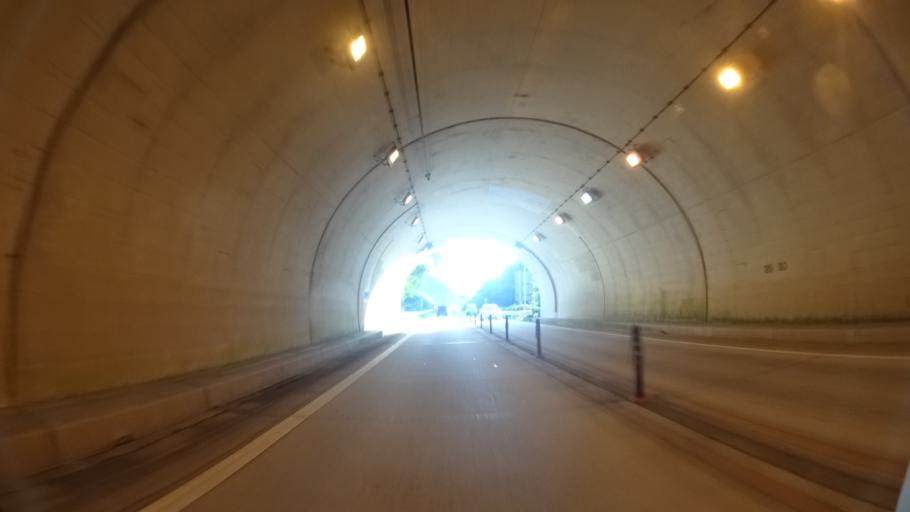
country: JP
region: Yamaguchi
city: Hagi
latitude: 34.3812
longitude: 131.3098
